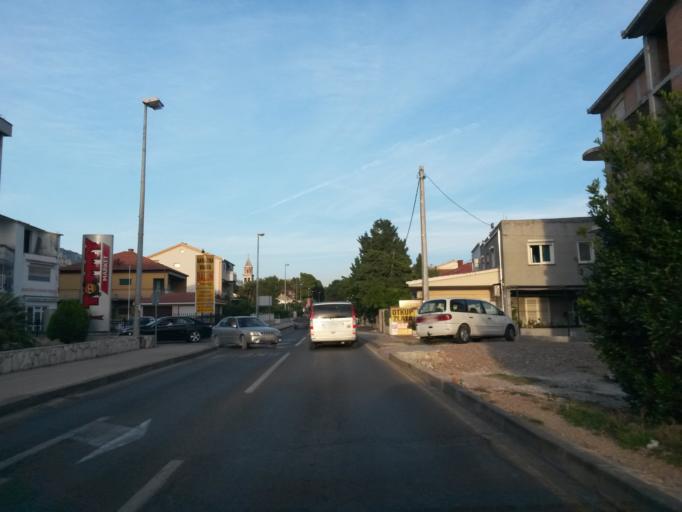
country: HR
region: Splitsko-Dalmatinska
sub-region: Grad Split
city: Split
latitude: 43.5493
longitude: 16.3932
